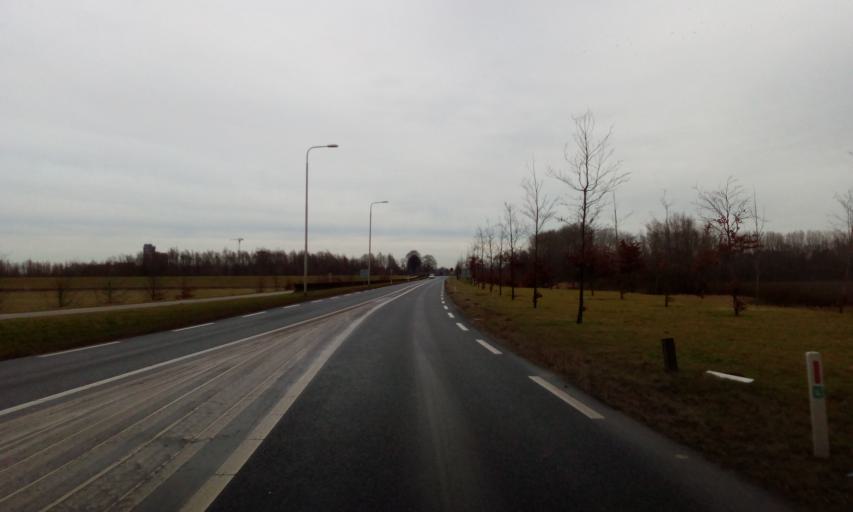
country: NL
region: North Brabant
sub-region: Gemeente Woudrichem
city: Woudrichem
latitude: 51.7910
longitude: 5.0413
